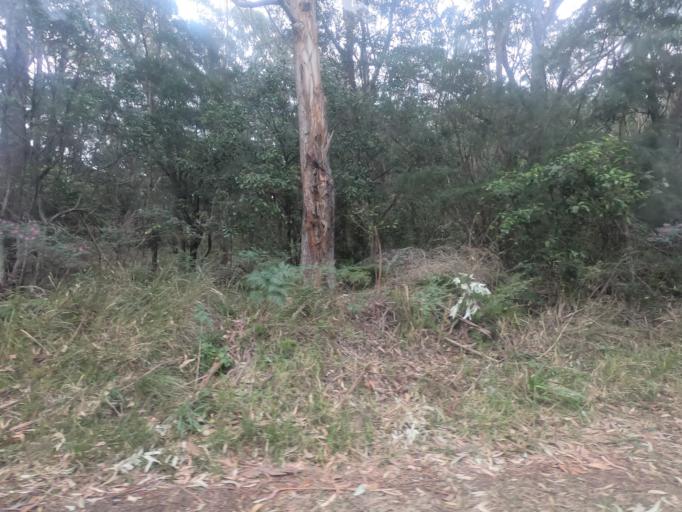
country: AU
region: New South Wales
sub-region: Wollongong
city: Bulli
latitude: -34.3001
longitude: 150.9303
